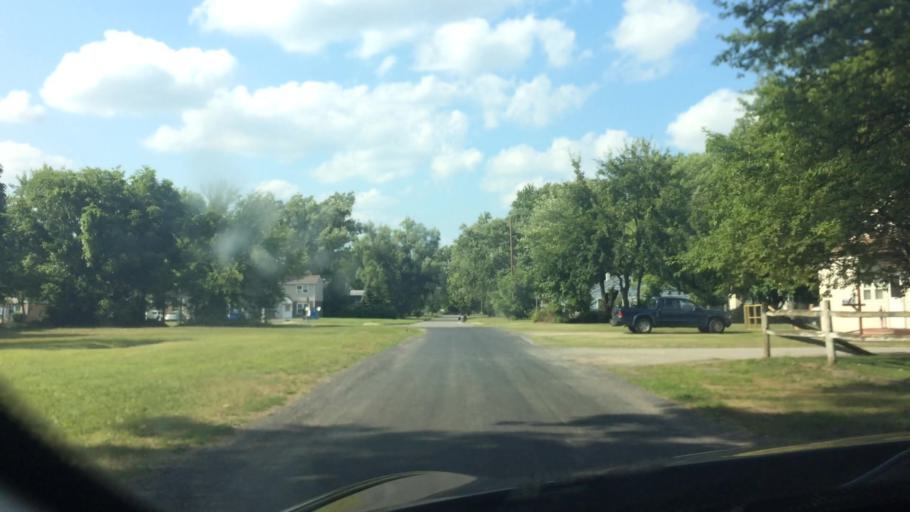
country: US
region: Ohio
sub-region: Lucas County
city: Ottawa Hills
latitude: 41.6264
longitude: -83.6209
